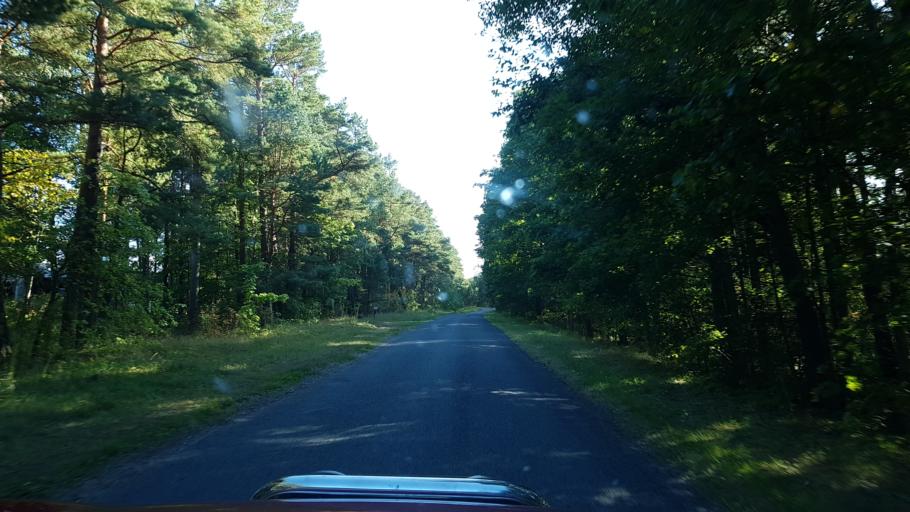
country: LV
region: Salacgrivas
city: Ainazi
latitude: 57.8934
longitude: 24.3714
